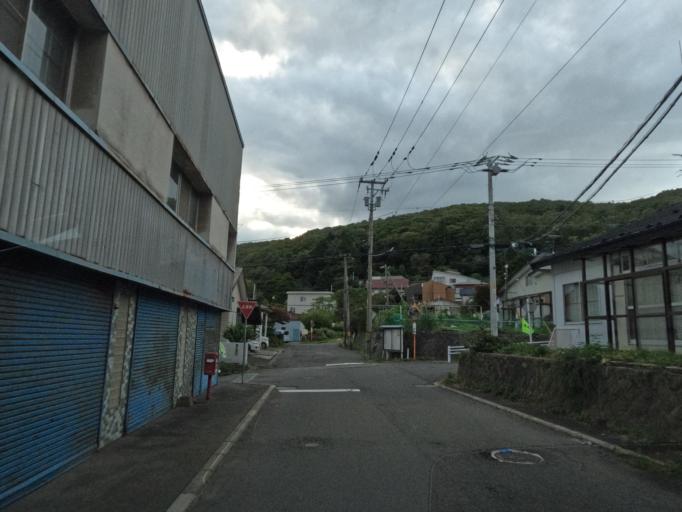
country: JP
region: Hokkaido
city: Muroran
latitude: 42.3643
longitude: 140.9652
